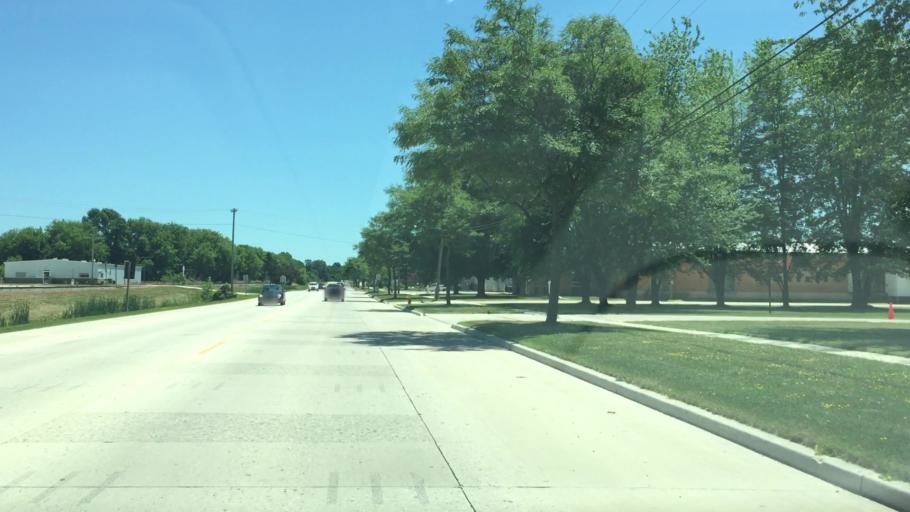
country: US
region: Wisconsin
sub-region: Calumet County
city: New Holstein
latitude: 43.9472
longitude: -88.0806
